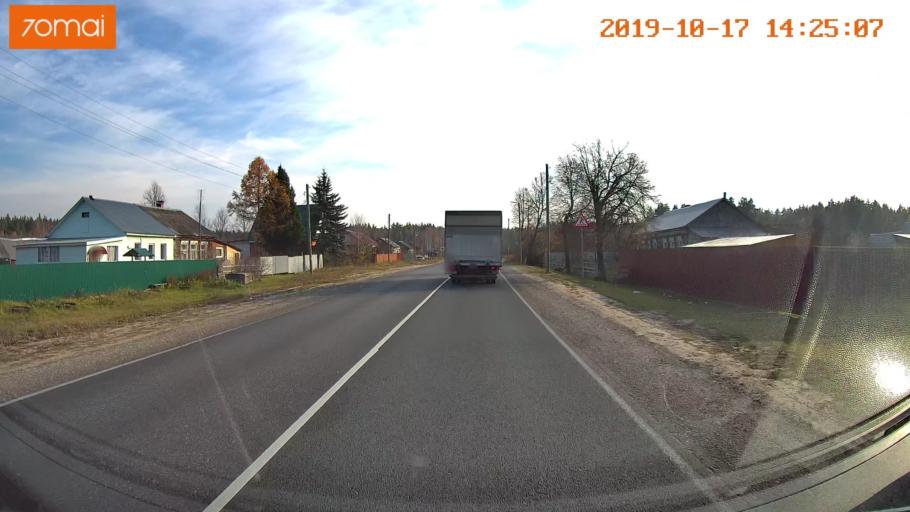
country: RU
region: Moskovskaya
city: Radovitskiy
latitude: 55.0035
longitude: 39.9749
